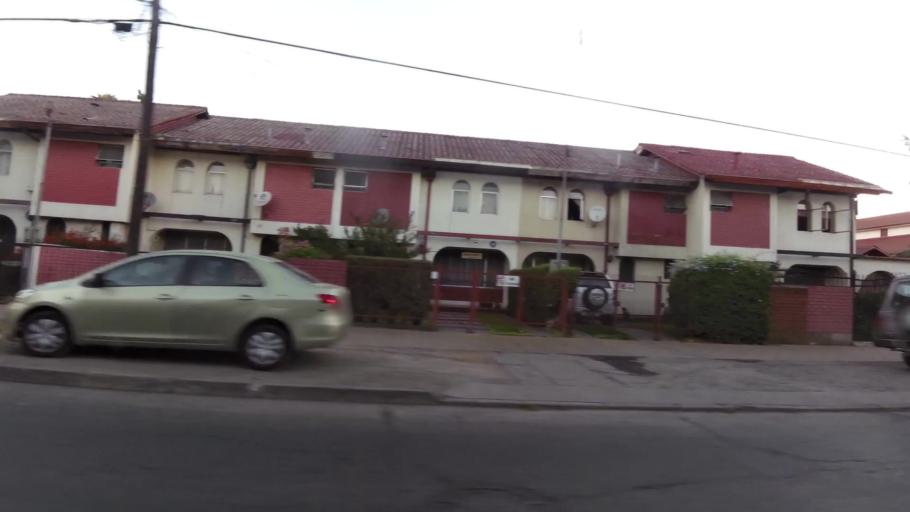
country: CL
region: Maule
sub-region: Provincia de Curico
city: Curico
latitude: -34.9893
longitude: -71.2375
